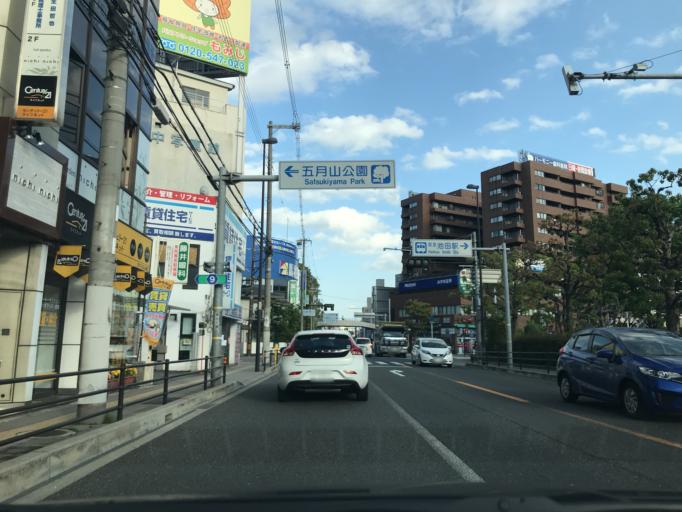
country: JP
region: Osaka
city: Ikeda
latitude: 34.8220
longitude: 135.4262
